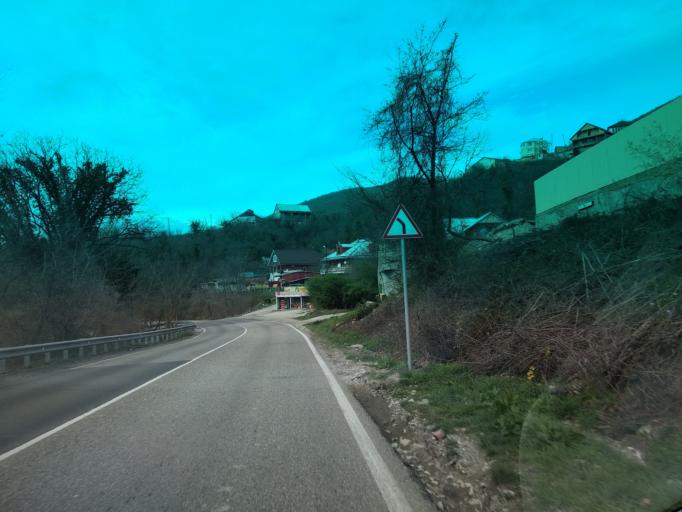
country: RU
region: Krasnodarskiy
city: Tuapse
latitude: 44.0891
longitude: 39.1232
